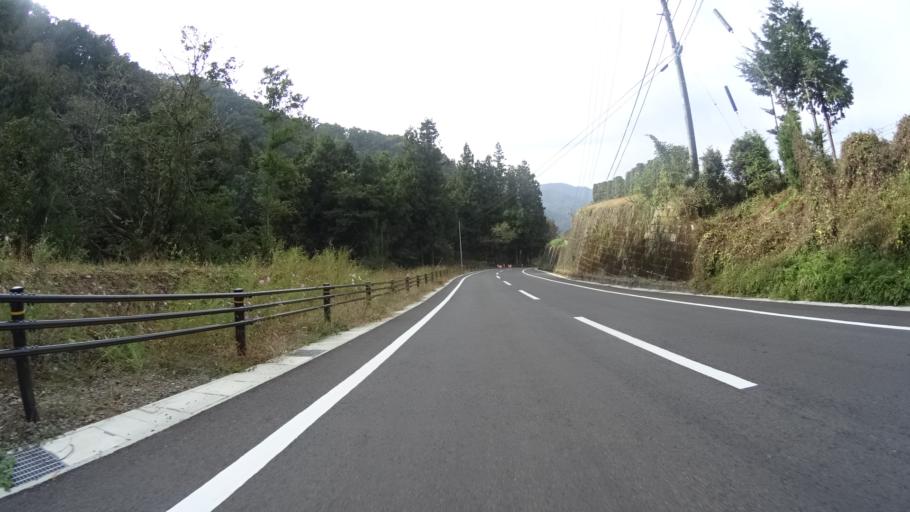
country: JP
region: Yamanashi
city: Otsuki
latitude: 35.6164
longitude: 139.0178
